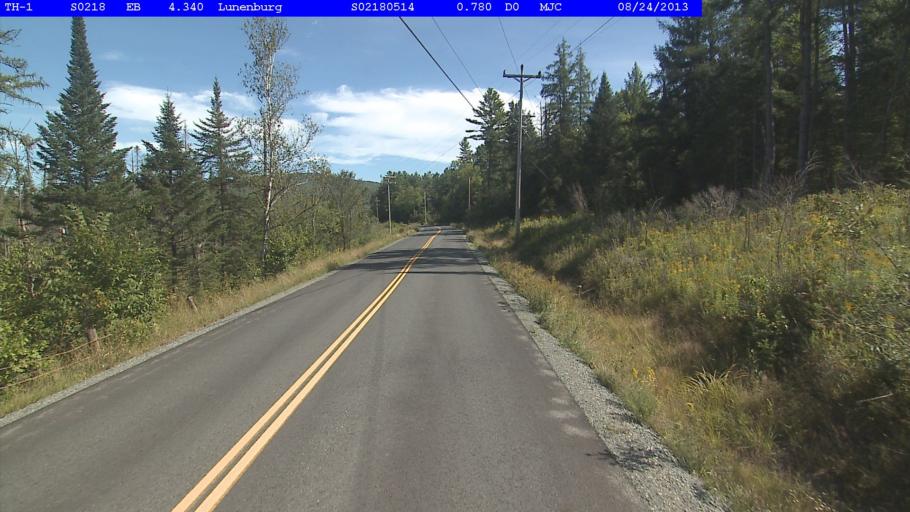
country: US
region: New Hampshire
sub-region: Grafton County
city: Littleton
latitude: 44.4136
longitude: -71.7360
